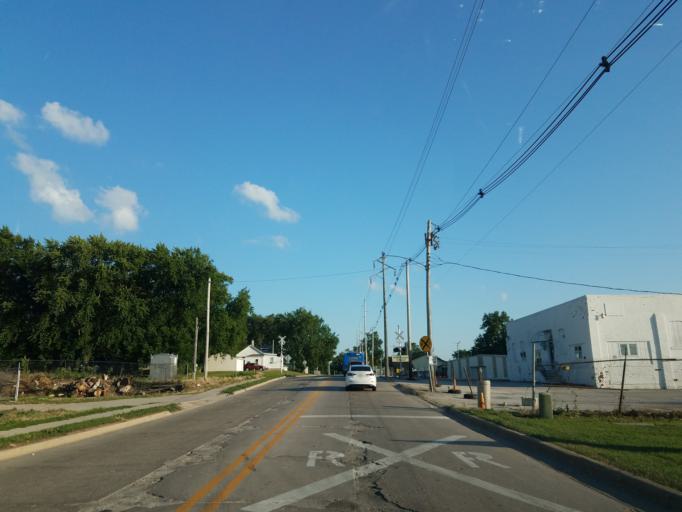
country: US
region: Illinois
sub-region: McLean County
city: Bloomington
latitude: 40.4786
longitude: -89.0164
